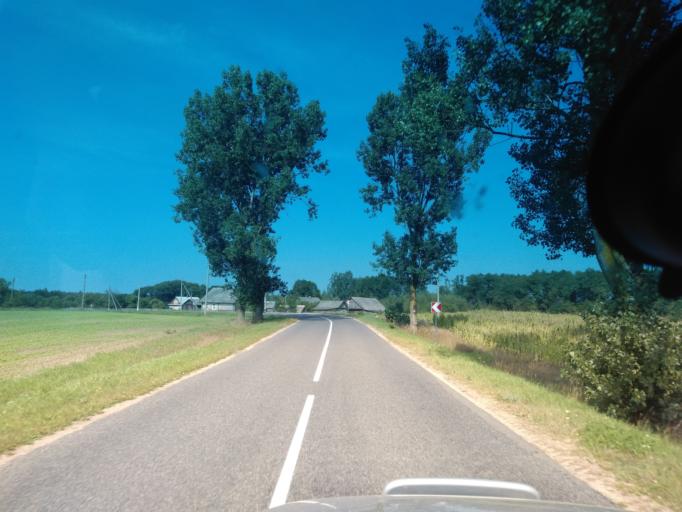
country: BY
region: Minsk
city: Kapyl'
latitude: 53.2729
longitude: 27.2098
